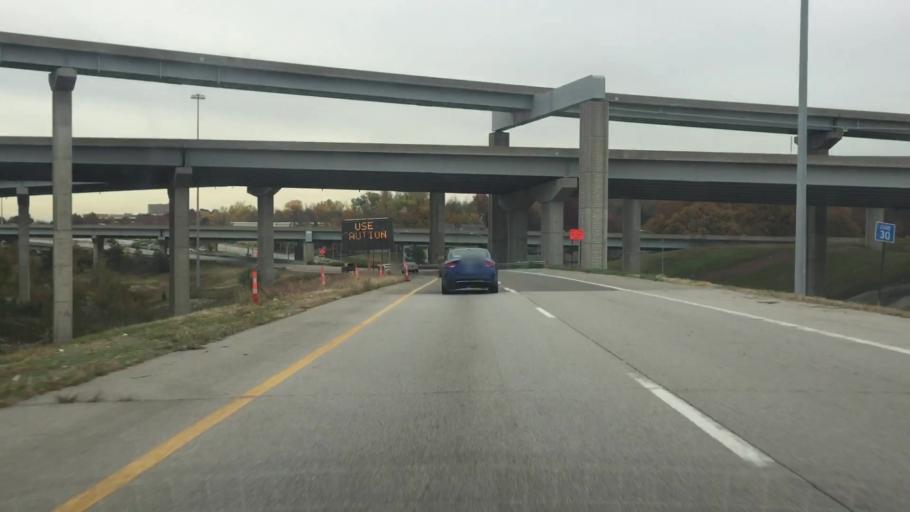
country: US
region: Missouri
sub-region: Jackson County
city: Grandview
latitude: 38.9316
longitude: -94.5267
